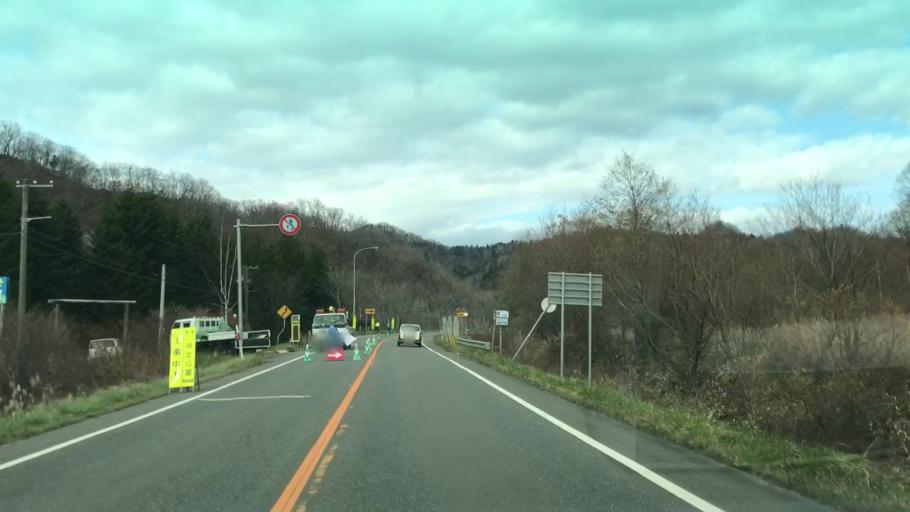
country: JP
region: Hokkaido
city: Shizunai-furukawacho
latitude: 42.7924
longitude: 142.3936
